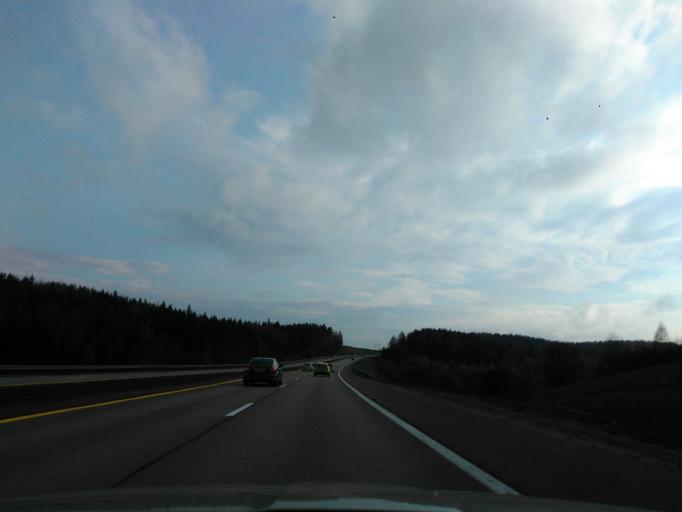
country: BY
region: Minsk
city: Lahoysk
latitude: 54.1092
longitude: 27.8021
